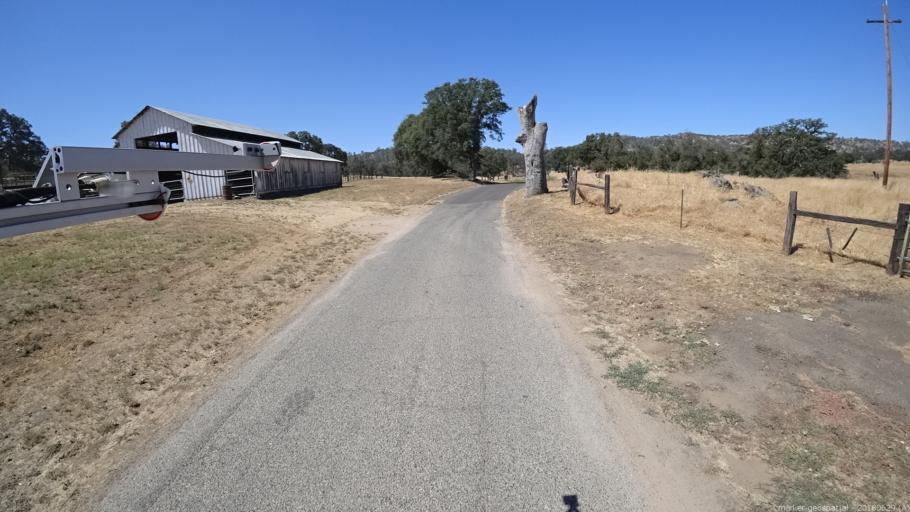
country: US
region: California
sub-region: Madera County
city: Yosemite Lakes
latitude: 37.1350
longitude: -119.7531
